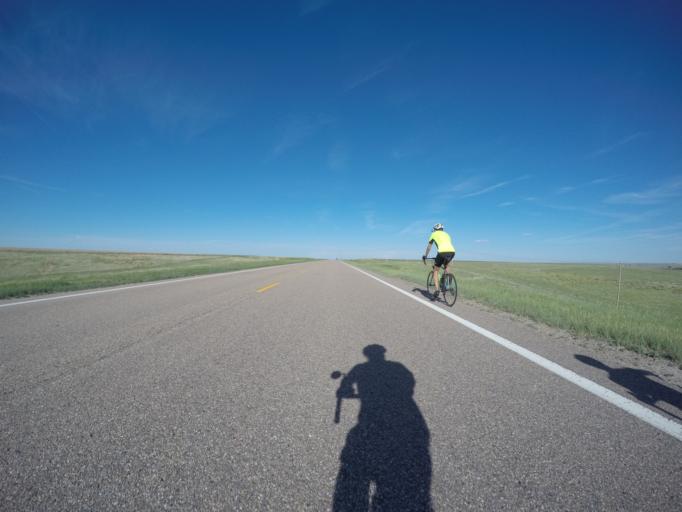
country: US
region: Kansas
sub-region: Cheyenne County
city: Saint Francis
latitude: 39.7570
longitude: -101.8935
